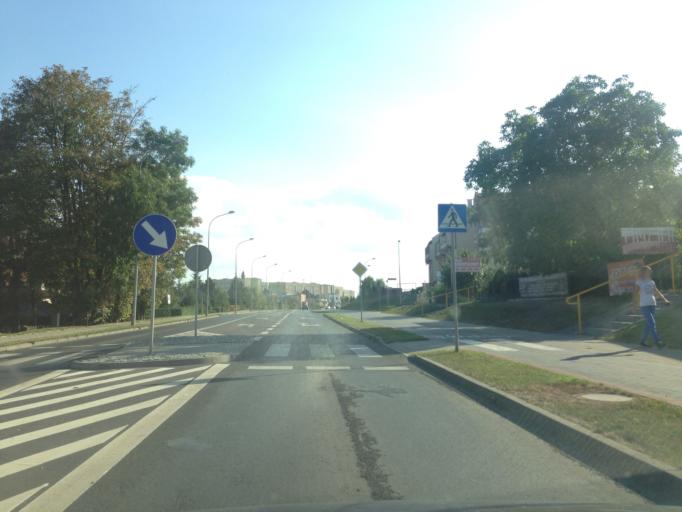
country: PL
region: Warmian-Masurian Voivodeship
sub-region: Powiat ilawski
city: Ilawa
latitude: 53.6081
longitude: 19.5691
